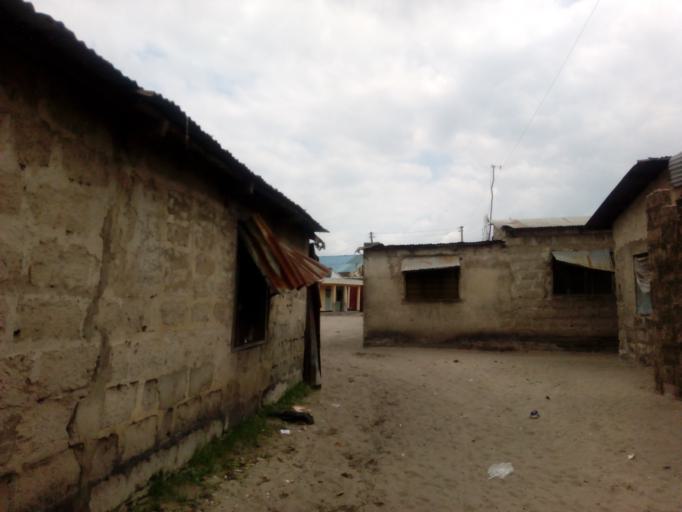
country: TZ
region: Dar es Salaam
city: Dar es Salaam
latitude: -6.8515
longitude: 39.2554
